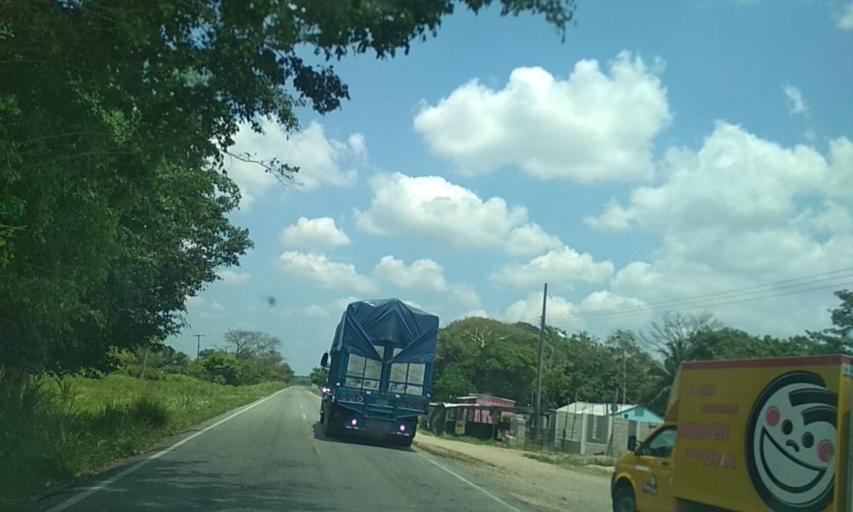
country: MX
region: Tabasco
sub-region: Huimanguillo
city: Huapacal 1ra. Seccion
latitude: 17.7539
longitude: -93.7245
